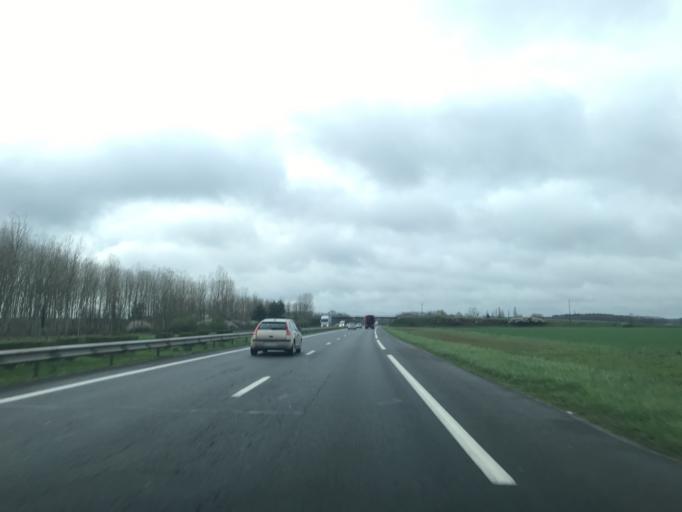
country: FR
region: Centre
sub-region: Departement du Loiret
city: Chateauneuf-sur-Loire
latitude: 47.8860
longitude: 2.2225
